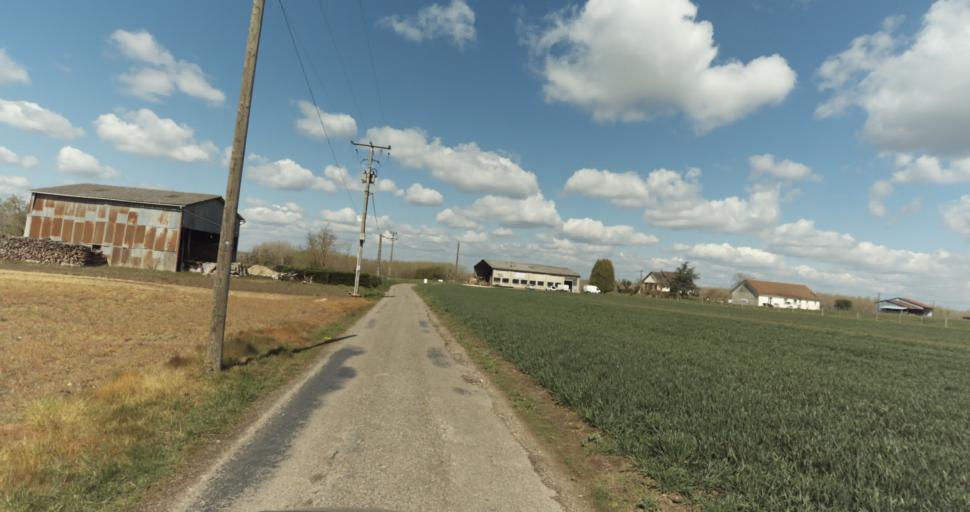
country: FR
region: Bourgogne
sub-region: Departement de la Cote-d'Or
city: Auxonne
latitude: 47.2141
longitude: 5.4181
